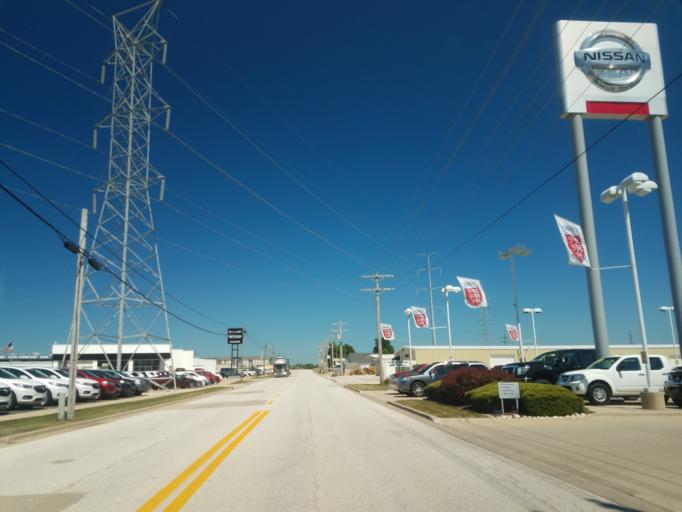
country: US
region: Illinois
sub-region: McLean County
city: Bloomington
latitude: 40.4594
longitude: -88.9661
